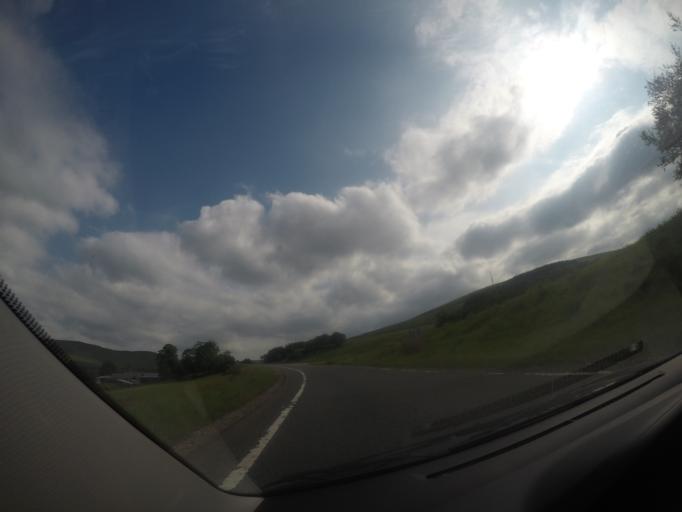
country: GB
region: Scotland
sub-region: South Lanarkshire
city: Douglas
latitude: 55.5029
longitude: -3.6944
